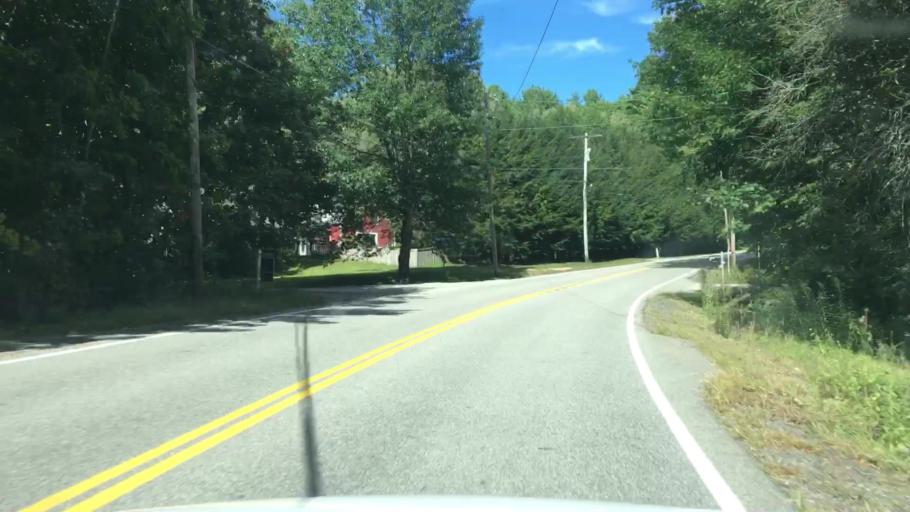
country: US
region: Maine
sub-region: Cumberland County
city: Westbrook
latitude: 43.6298
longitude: -70.4087
